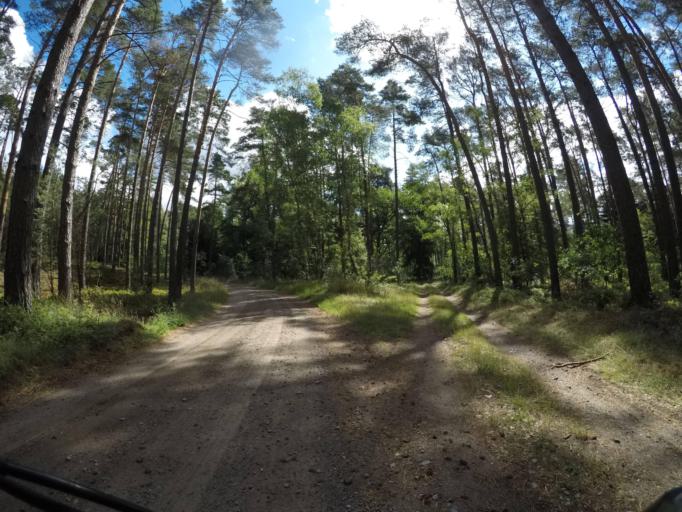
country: DE
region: Lower Saxony
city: Hitzacker
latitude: 53.2324
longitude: 11.0207
